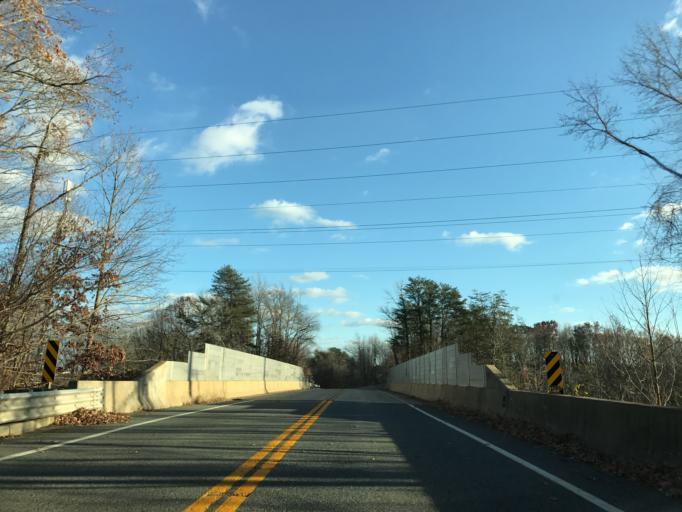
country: US
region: Maryland
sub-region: Harford County
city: Edgewood
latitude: 39.4048
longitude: -76.3205
